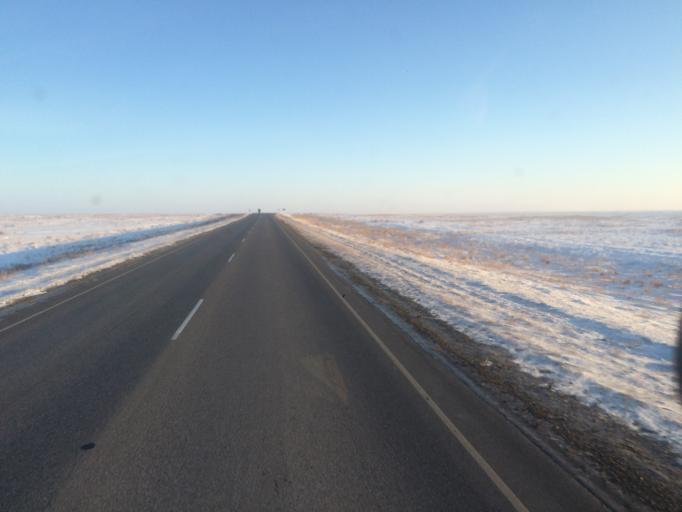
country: KZ
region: Aqtoebe
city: Yrghyz
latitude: 47.9606
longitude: 61.2567
